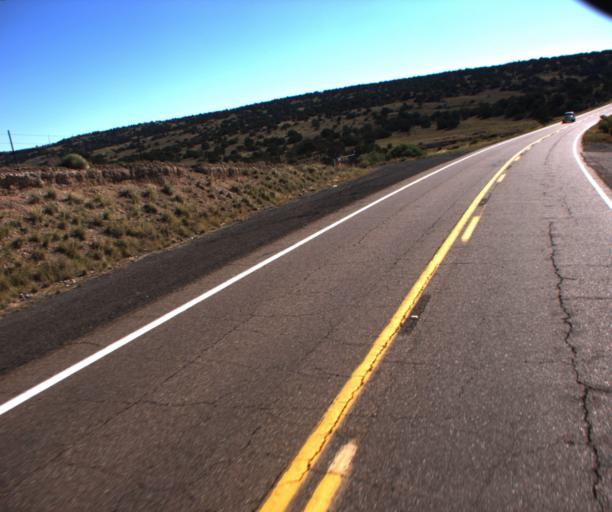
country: US
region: Arizona
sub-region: Apache County
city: Saint Johns
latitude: 34.4861
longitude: -109.5788
